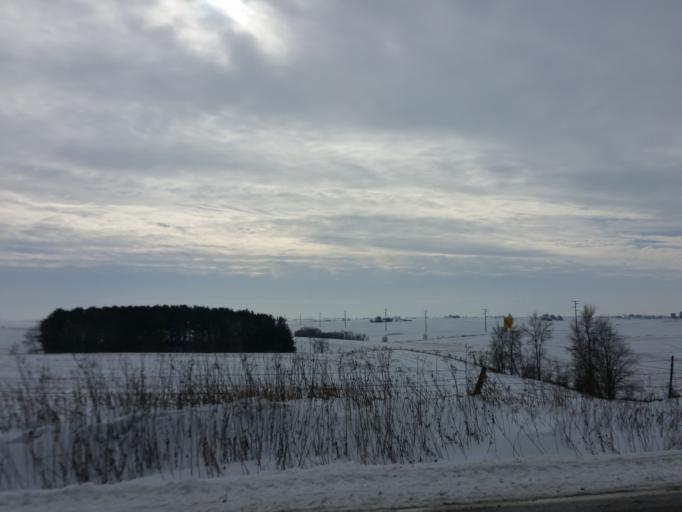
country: US
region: Iowa
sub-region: Dubuque County
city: Peosta
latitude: 42.3966
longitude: -90.8344
